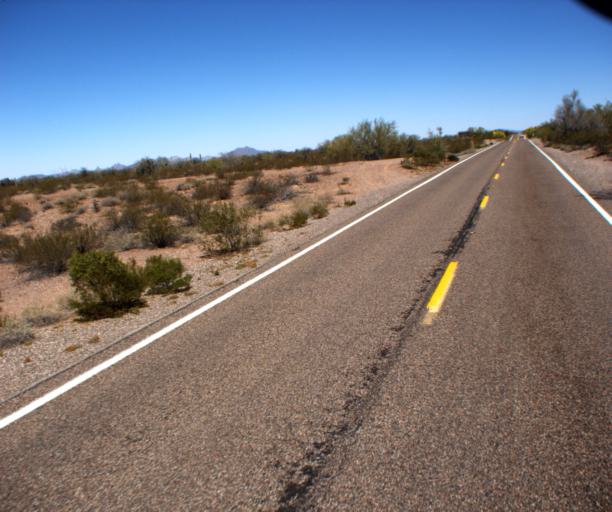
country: US
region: Arizona
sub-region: Pima County
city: Ajo
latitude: 32.1373
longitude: -112.7668
